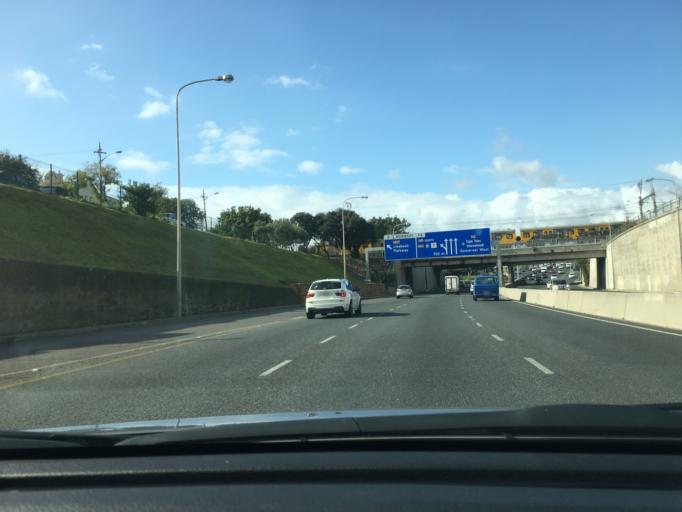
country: ZA
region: Western Cape
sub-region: City of Cape Town
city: Rosebank
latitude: -33.9447
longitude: 18.4721
